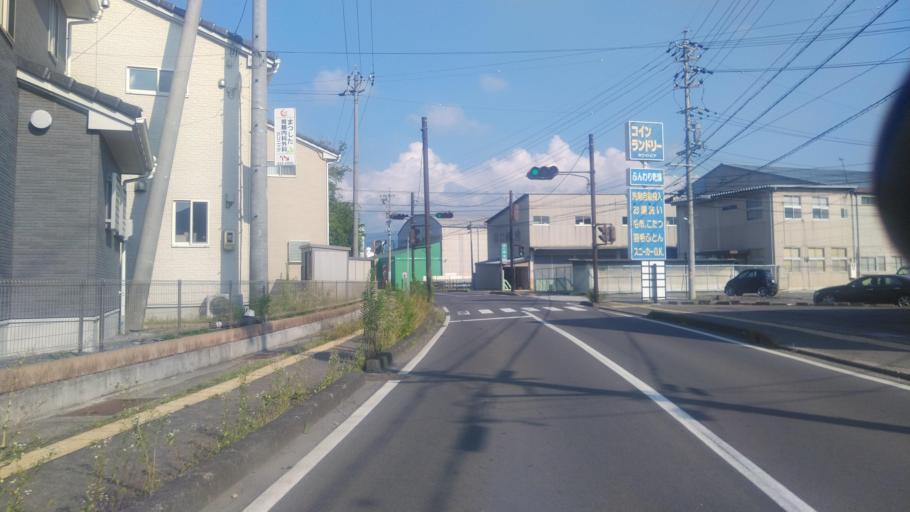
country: JP
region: Nagano
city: Nagano-shi
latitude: 36.6281
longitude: 138.2151
